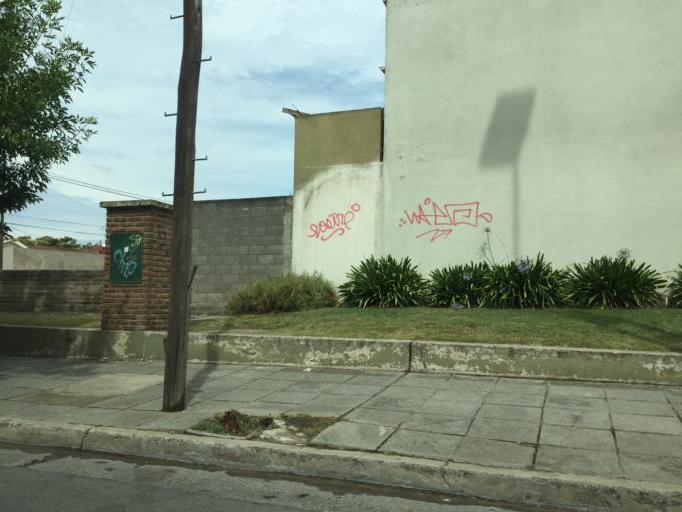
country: AR
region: Buenos Aires
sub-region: Partido de Tandil
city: Tandil
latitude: -37.3231
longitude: -59.1096
